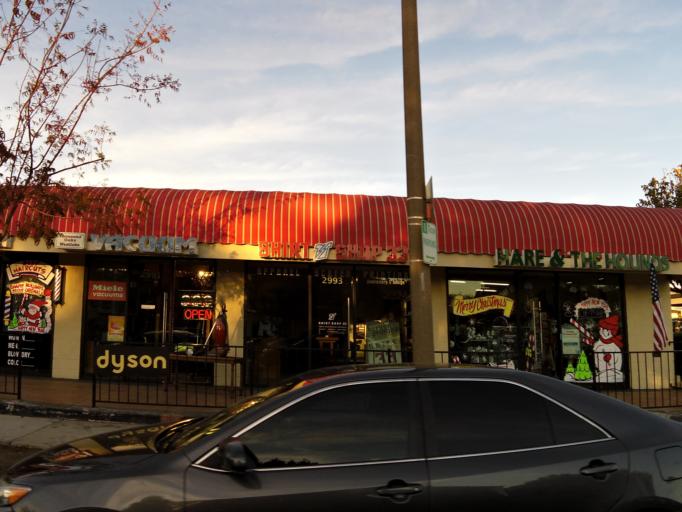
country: US
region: California
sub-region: Ventura County
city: Thousand Oaks
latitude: 34.1700
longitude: -118.8371
